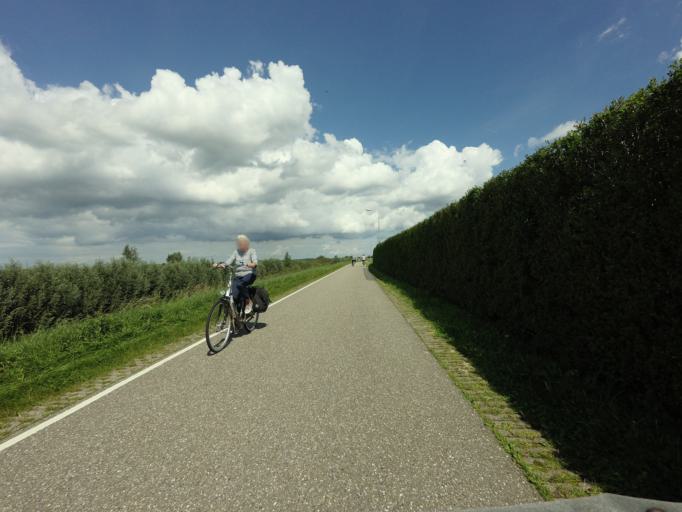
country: NL
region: Utrecht
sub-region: Gemeente IJsselstein
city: IJsselstein
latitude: 51.9692
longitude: 5.0440
